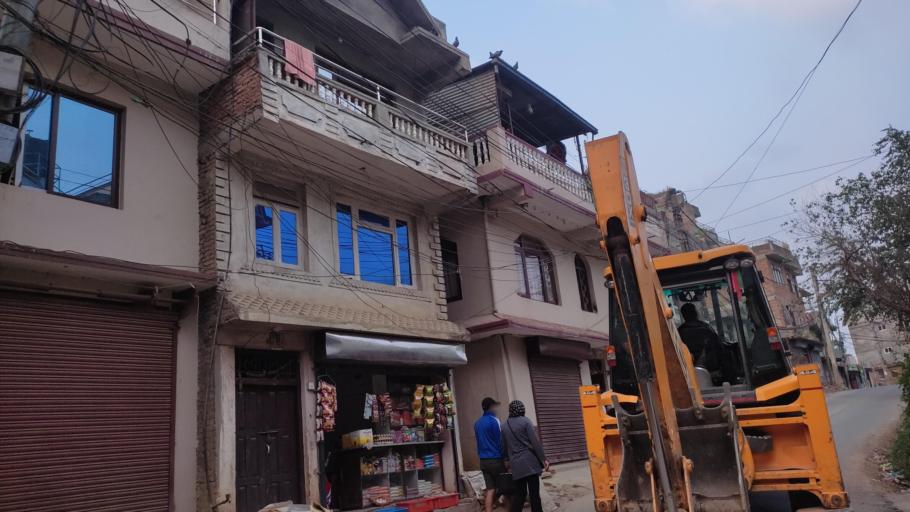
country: NP
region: Central Region
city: Kirtipur
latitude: 27.6670
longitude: 85.2509
